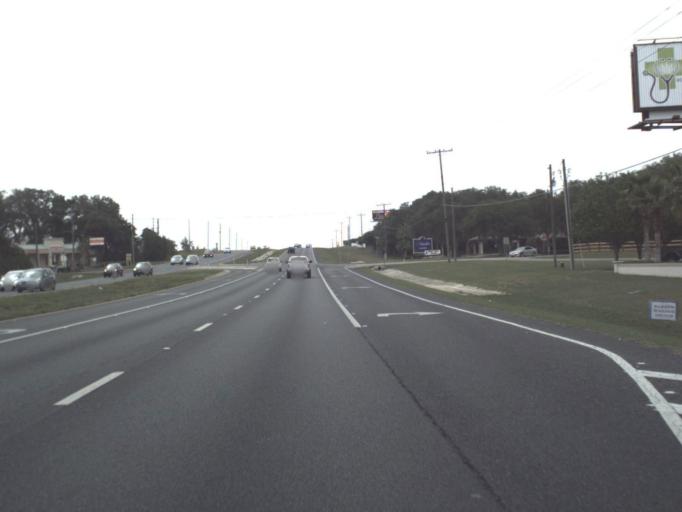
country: US
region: Florida
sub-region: Sumter County
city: The Villages
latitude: 28.9756
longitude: -81.9812
